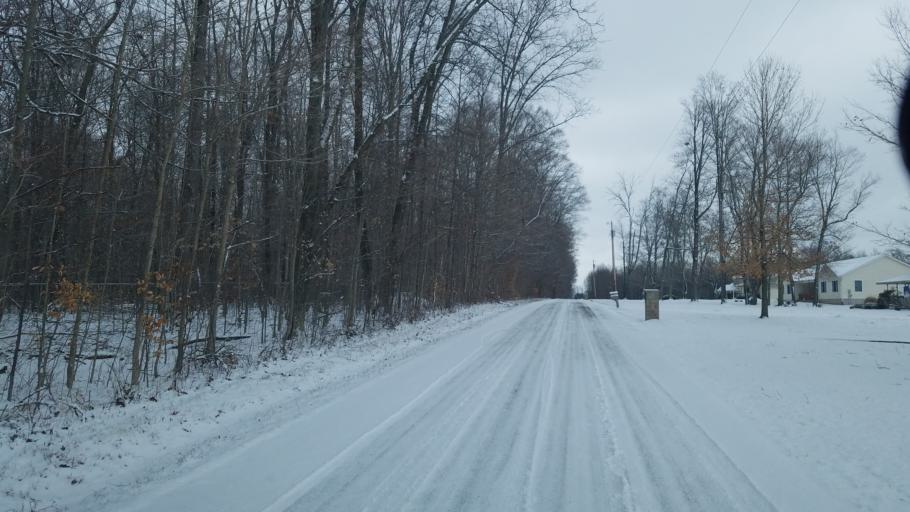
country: US
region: Ohio
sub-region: Knox County
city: Fredericktown
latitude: 40.5427
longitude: -82.5828
